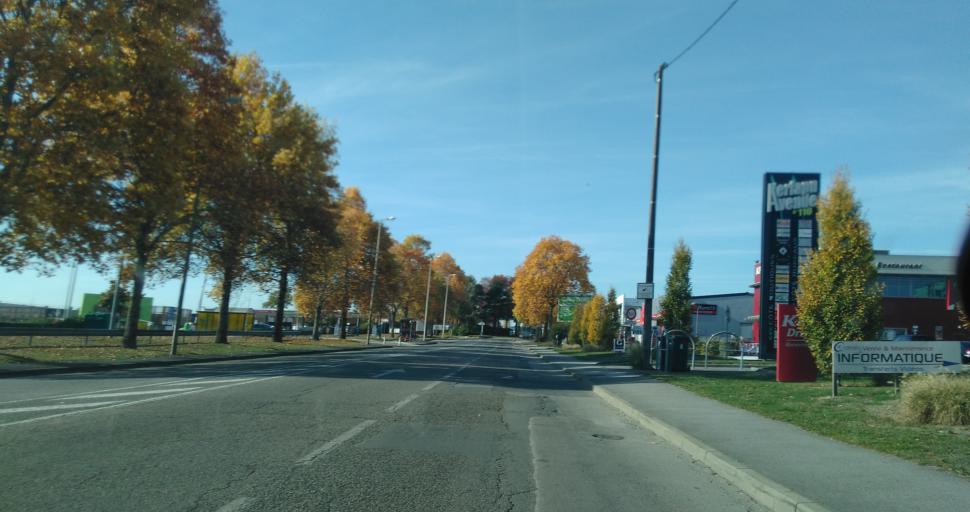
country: FR
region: Brittany
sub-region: Departement du Morbihan
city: Vannes
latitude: 47.6600
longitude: -2.7874
